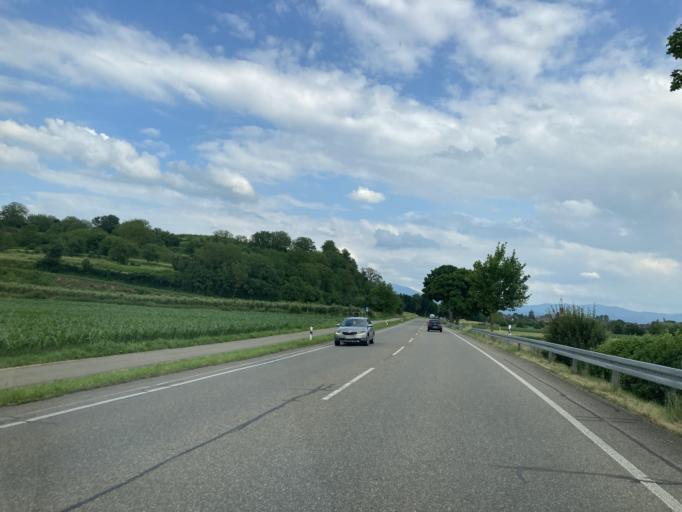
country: DE
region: Baden-Wuerttemberg
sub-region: Freiburg Region
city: Teningen
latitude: 48.1432
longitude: 7.7954
